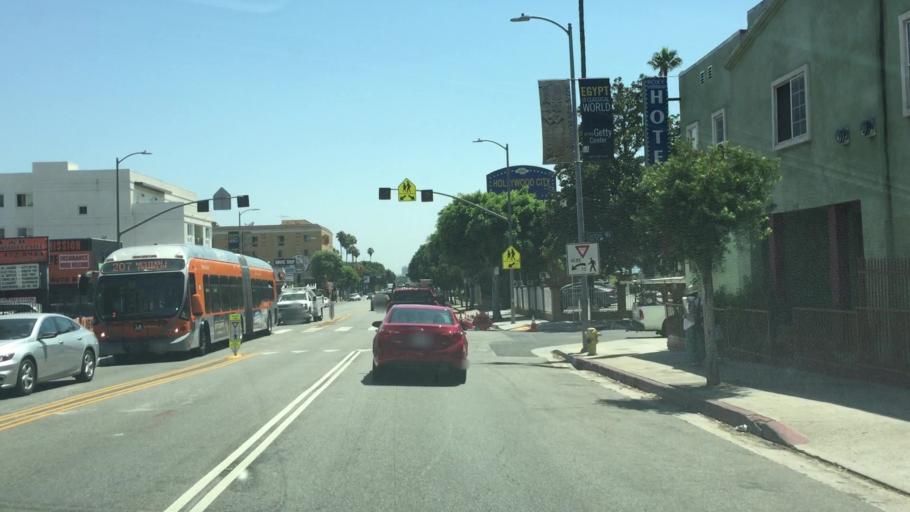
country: US
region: California
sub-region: Los Angeles County
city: Hollywood
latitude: 34.1008
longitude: -118.3094
